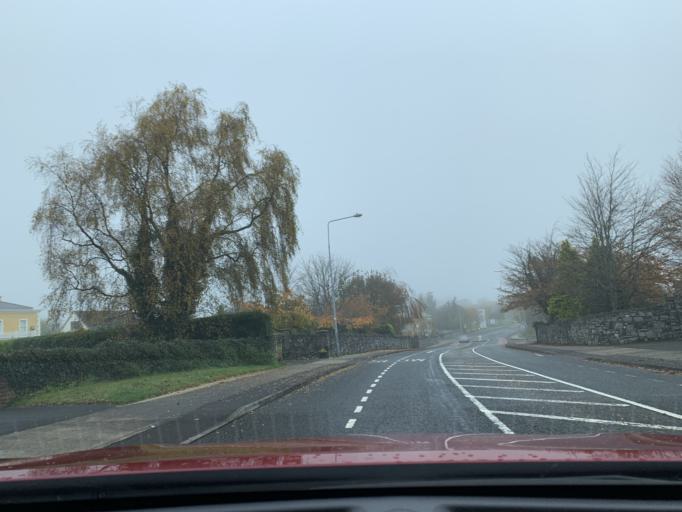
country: IE
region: Connaught
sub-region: Sligo
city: Sligo
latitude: 54.2748
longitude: -8.5041
